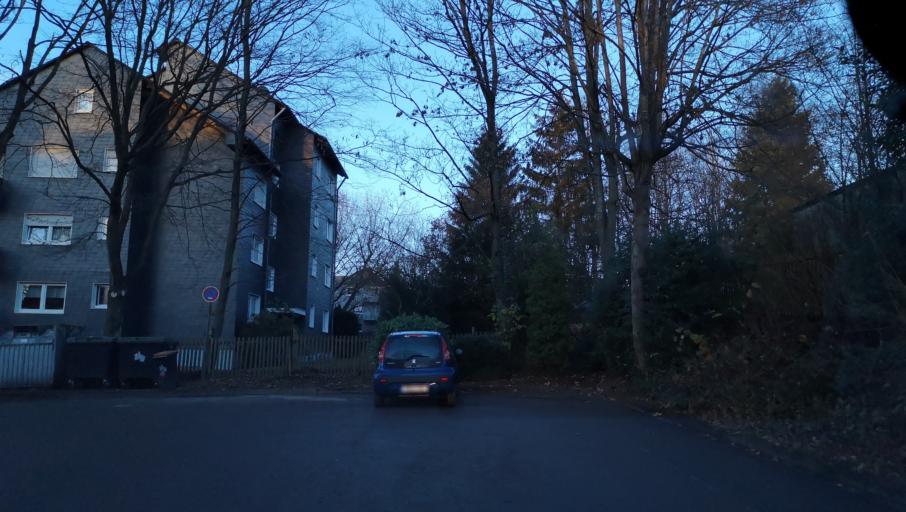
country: DE
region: North Rhine-Westphalia
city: Radevormwald
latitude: 51.1980
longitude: 7.3614
